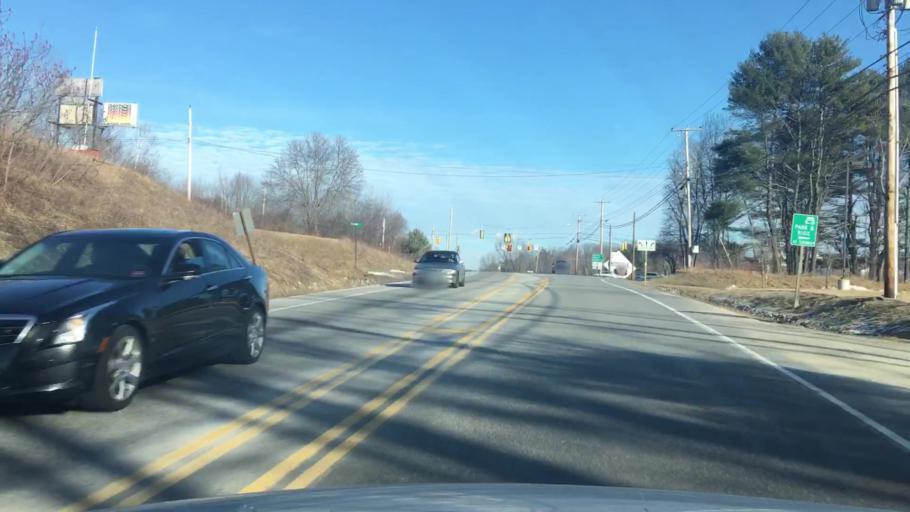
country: US
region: Maine
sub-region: Androscoggin County
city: Sabattus
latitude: 44.1147
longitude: -70.1046
